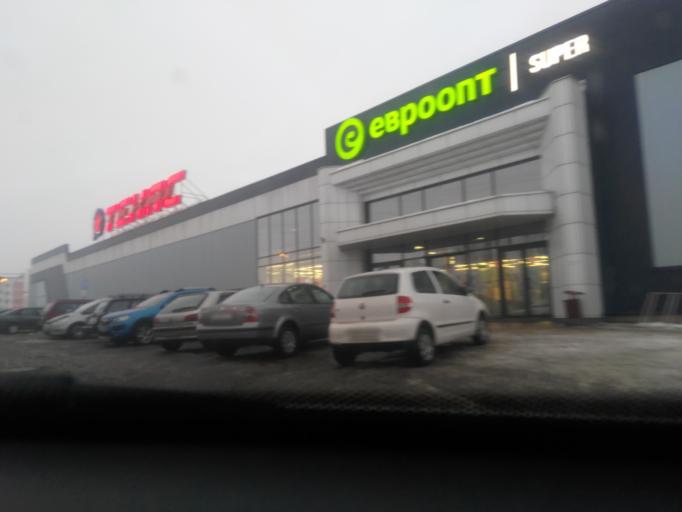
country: BY
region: Mogilev
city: Babruysk
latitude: 53.1987
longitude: 29.2228
